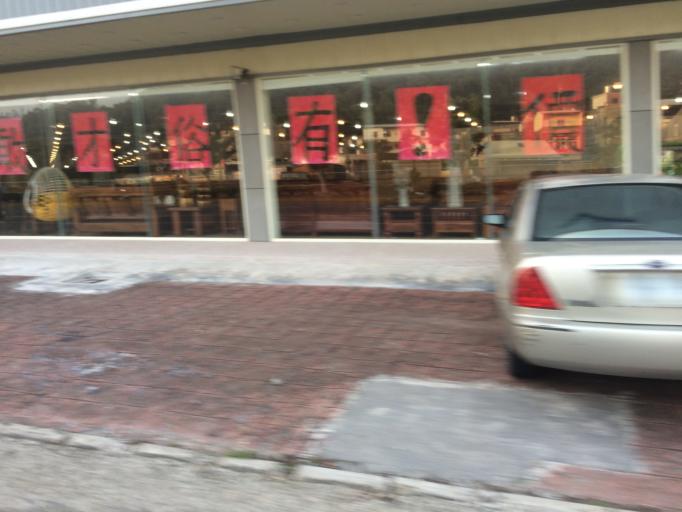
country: TW
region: Taiwan
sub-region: Hsinchu
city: Hsinchu
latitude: 24.7804
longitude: 120.9189
